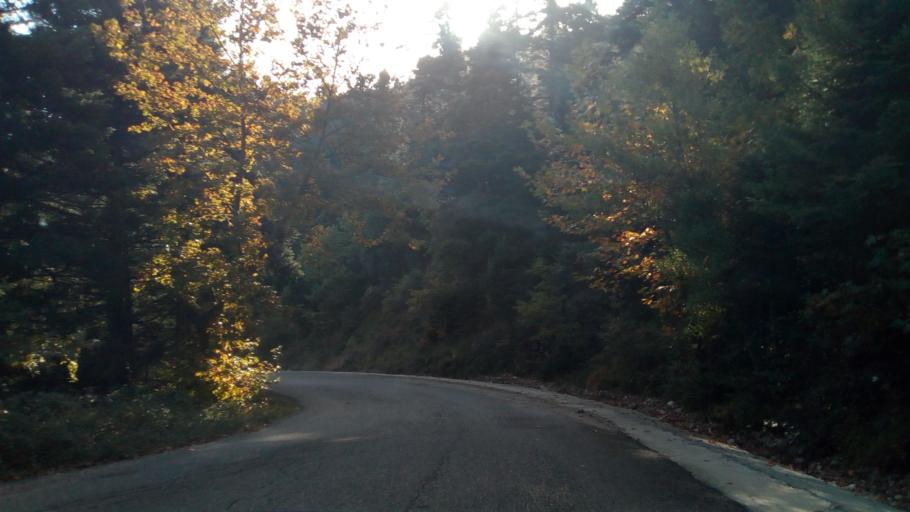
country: GR
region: West Greece
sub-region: Nomos Aitolias kai Akarnanias
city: Thermo
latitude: 38.6456
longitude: 21.8487
